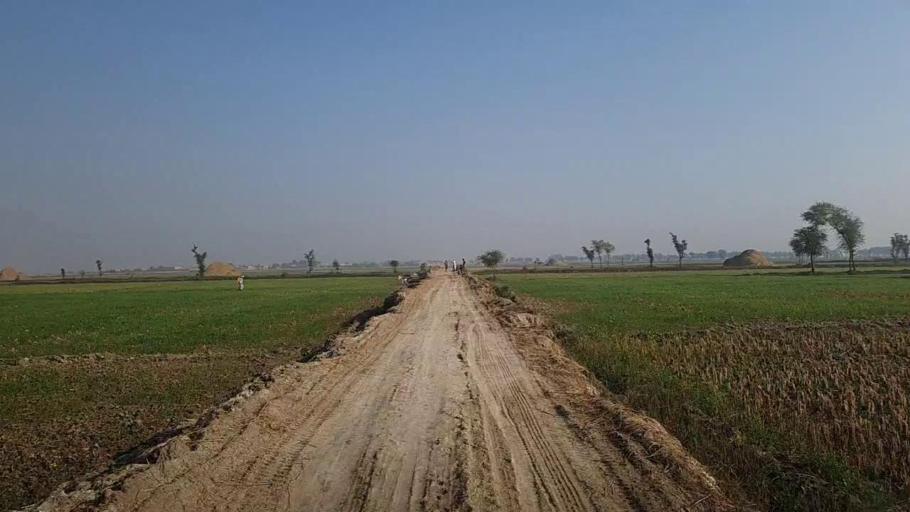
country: PK
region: Sindh
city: Sita Road
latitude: 27.1116
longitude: 67.8926
